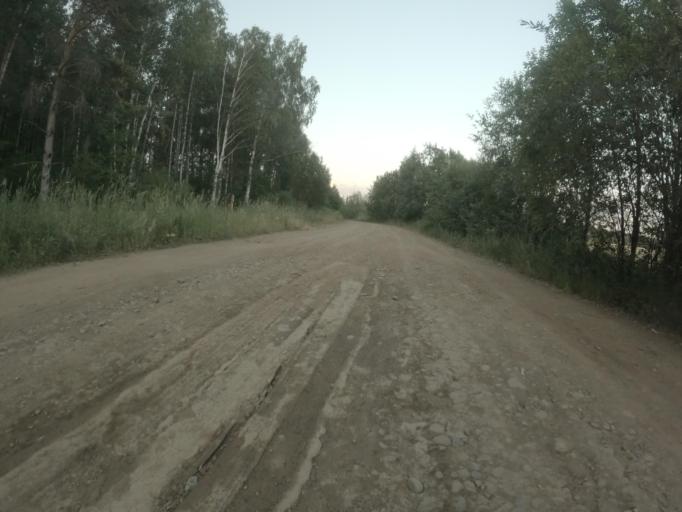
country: RU
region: Leningrad
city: Yanino Vtoroye
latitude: 59.9583
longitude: 30.5590
